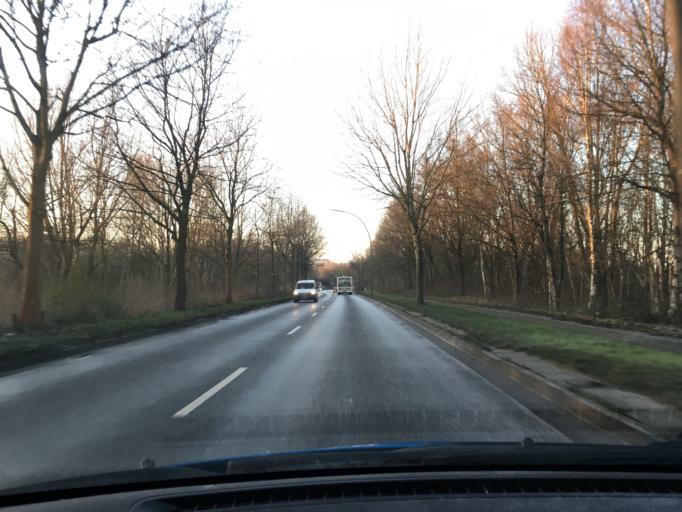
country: DE
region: Hamburg
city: Harburg
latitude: 53.4803
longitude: 9.9202
